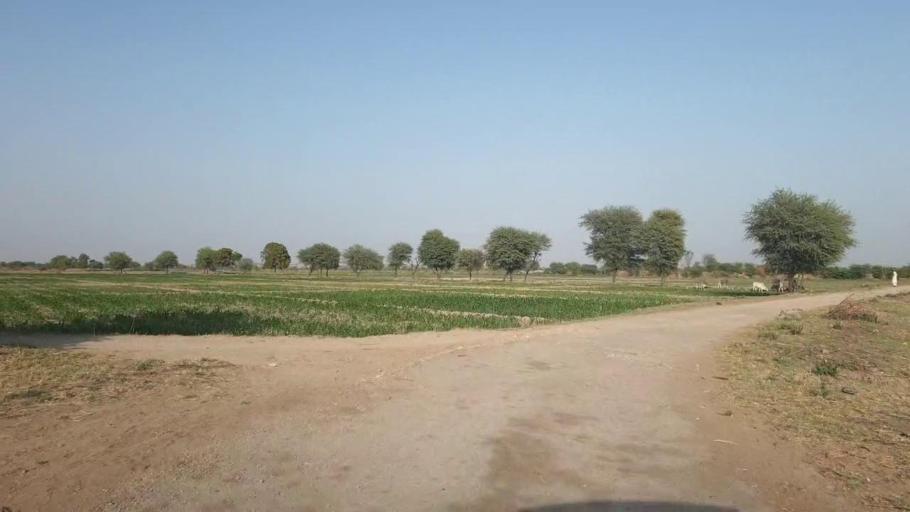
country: PK
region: Sindh
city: Dhoro Naro
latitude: 25.4949
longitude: 69.5764
